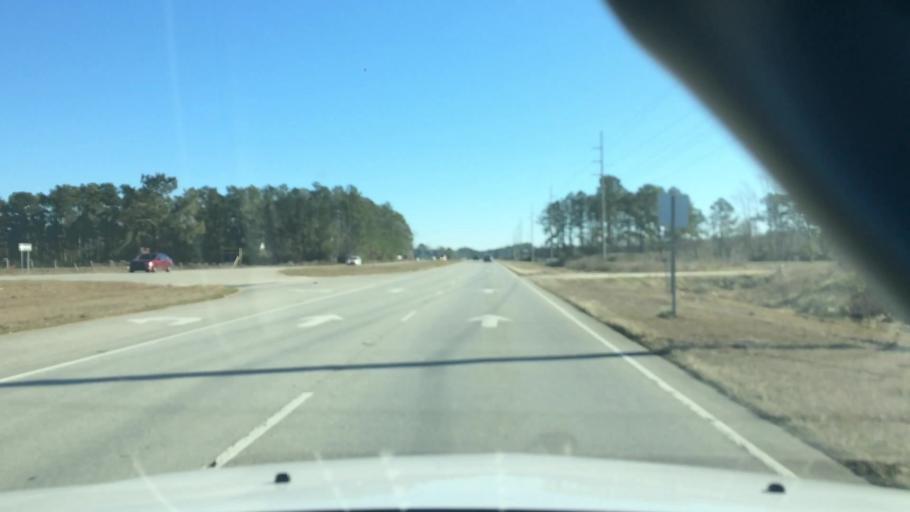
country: US
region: North Carolina
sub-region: Brunswick County
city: Shallotte
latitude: 33.9557
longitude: -78.4409
